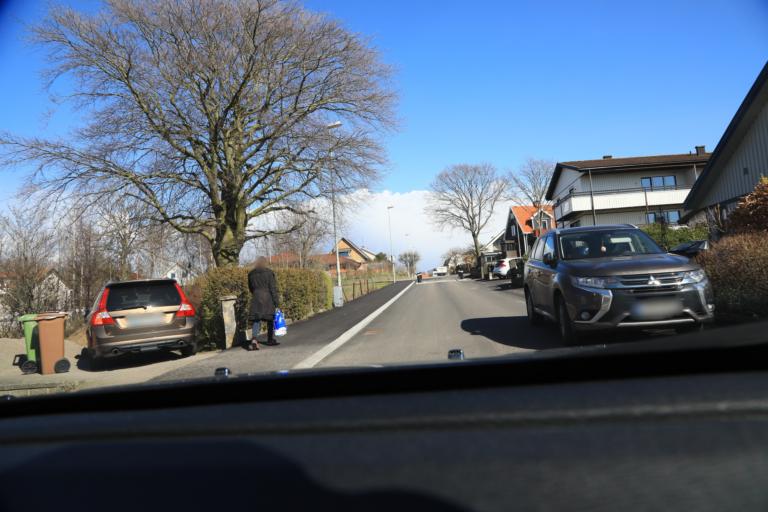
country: SE
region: Halland
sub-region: Varbergs Kommun
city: Varberg
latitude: 57.1024
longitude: 12.2744
